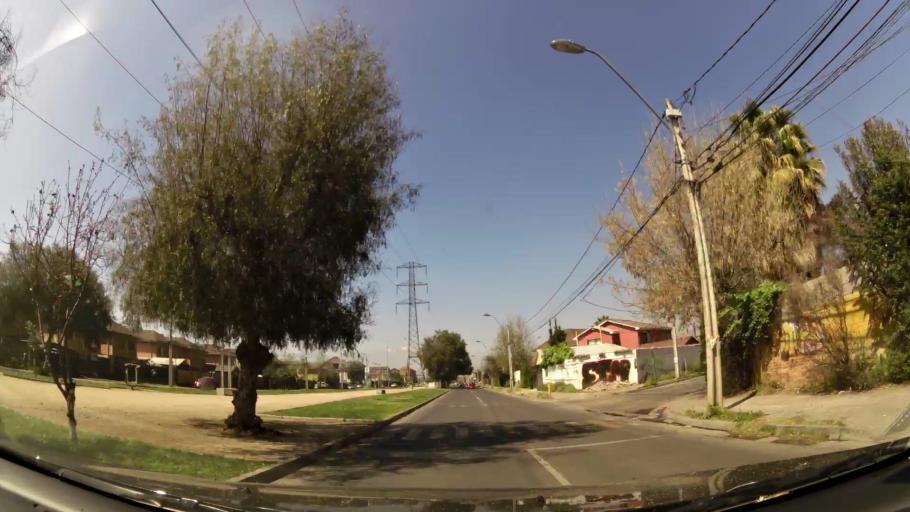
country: CL
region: Santiago Metropolitan
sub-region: Provincia de Santiago
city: Lo Prado
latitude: -33.3597
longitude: -70.7236
